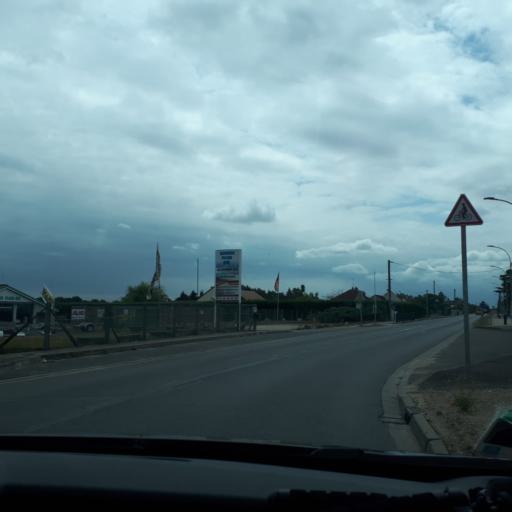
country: FR
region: Centre
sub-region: Departement du Loiret
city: Saint-Pere-sur-Loire
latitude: 47.7889
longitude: 2.3784
